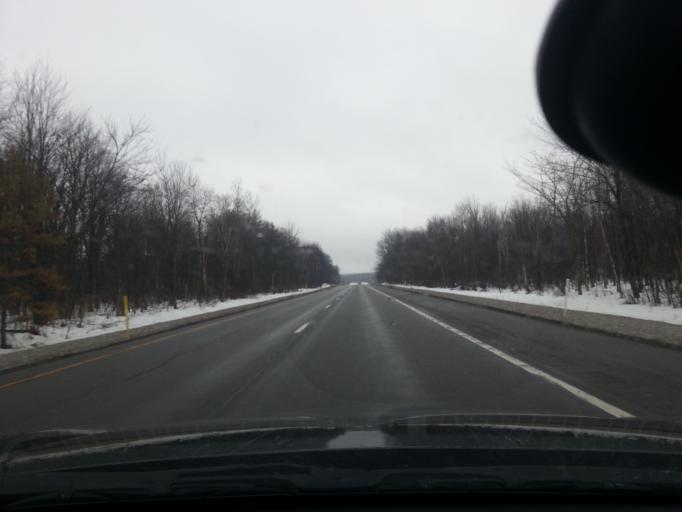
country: US
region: New York
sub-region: Jefferson County
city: Adams
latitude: 43.7860
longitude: -76.0429
